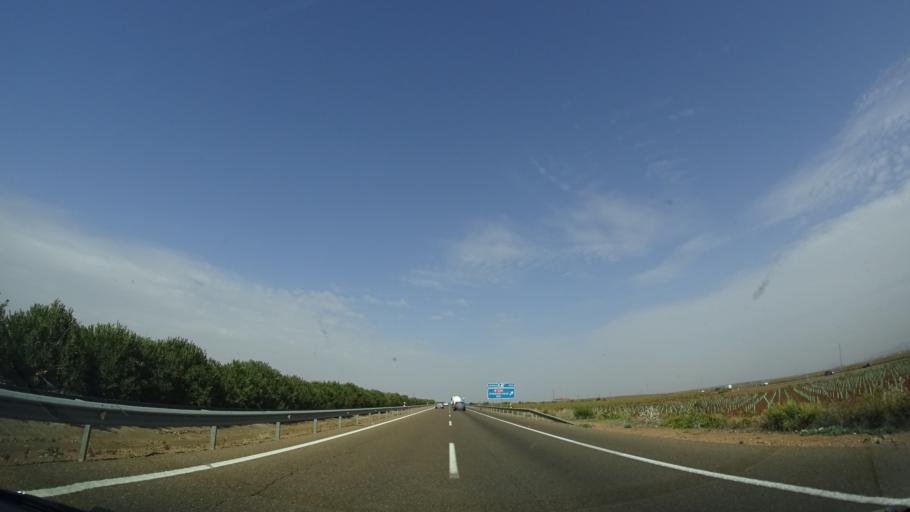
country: ES
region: Extremadura
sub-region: Provincia de Badajoz
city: Almendralejo
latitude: 38.6467
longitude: -6.3763
